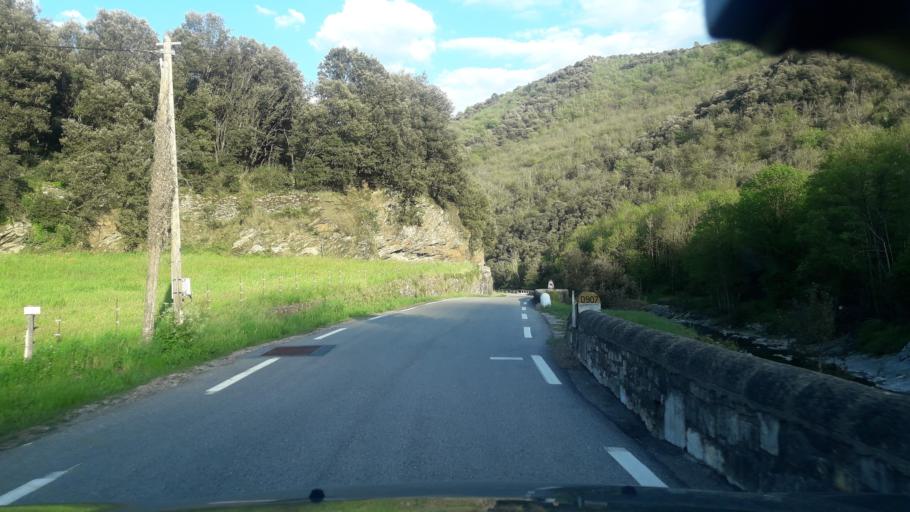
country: FR
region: Languedoc-Roussillon
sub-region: Departement du Gard
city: Valleraugue
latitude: 44.1379
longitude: 3.7353
